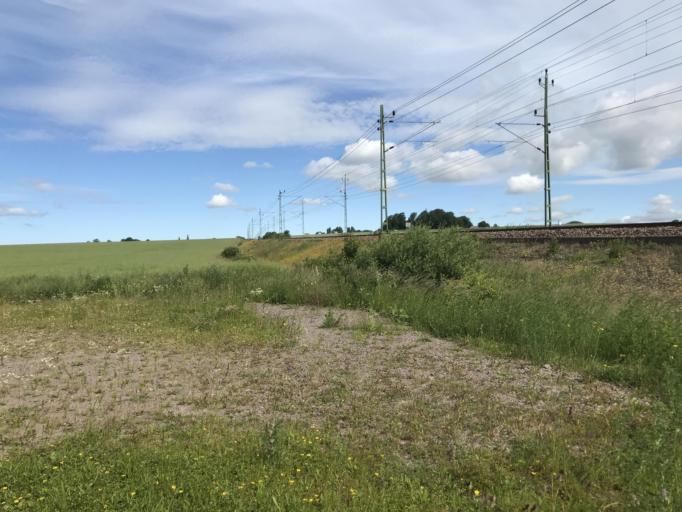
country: SE
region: Skane
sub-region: Helsingborg
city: Glumslov
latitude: 55.9263
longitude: 12.8260
